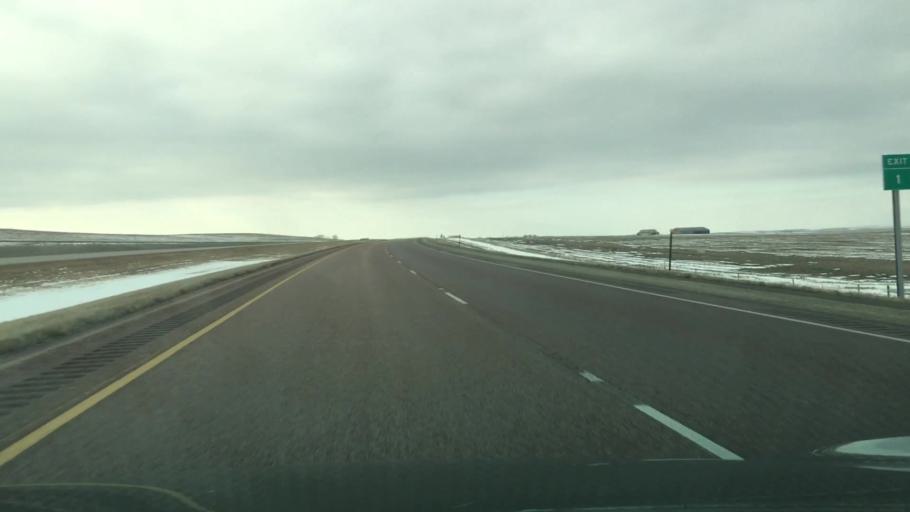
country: US
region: South Dakota
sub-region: Lyman County
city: Kennebec
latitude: 43.8697
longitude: -99.7160
